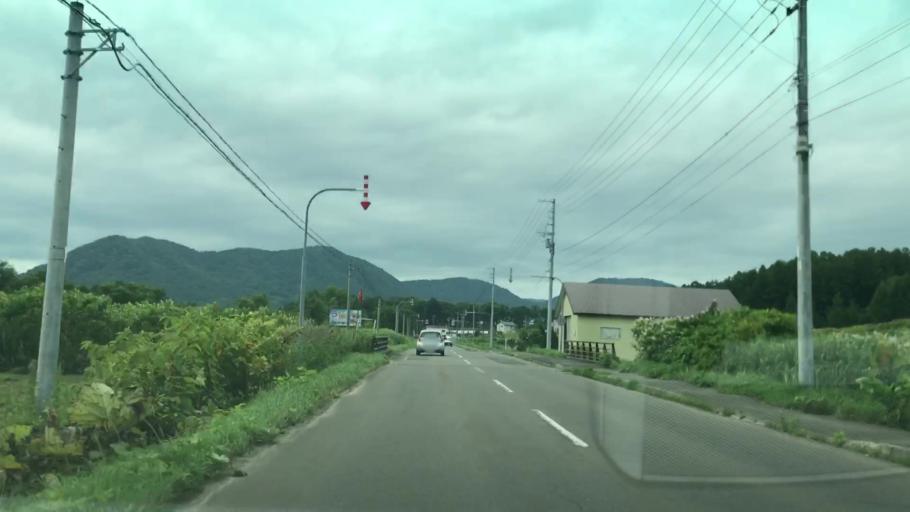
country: JP
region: Hokkaido
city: Yoichi
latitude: 43.0919
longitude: 140.8179
